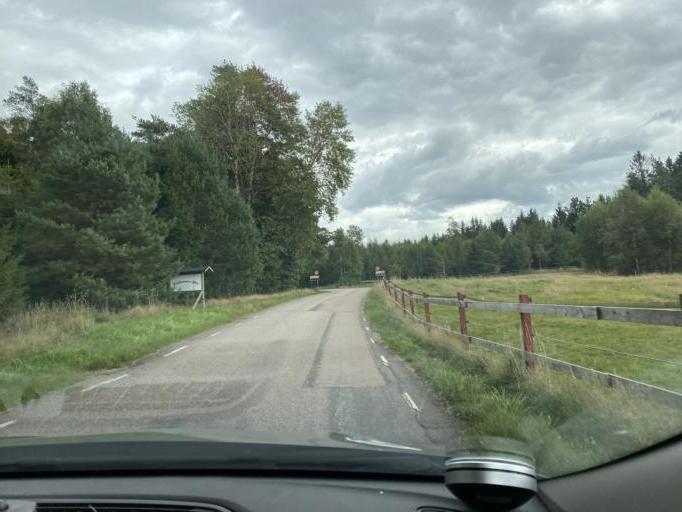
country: SE
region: Kronoberg
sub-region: Markaryds Kommun
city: Markaryd
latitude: 56.4875
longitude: 13.5381
